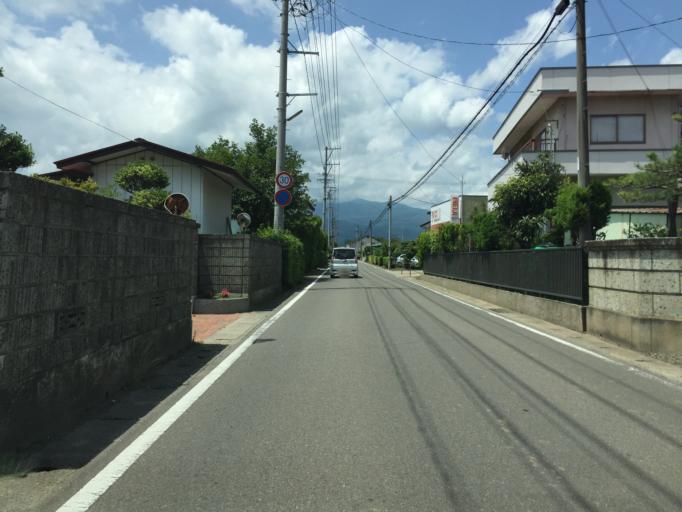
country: JP
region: Fukushima
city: Fukushima-shi
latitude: 37.7719
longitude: 140.4193
